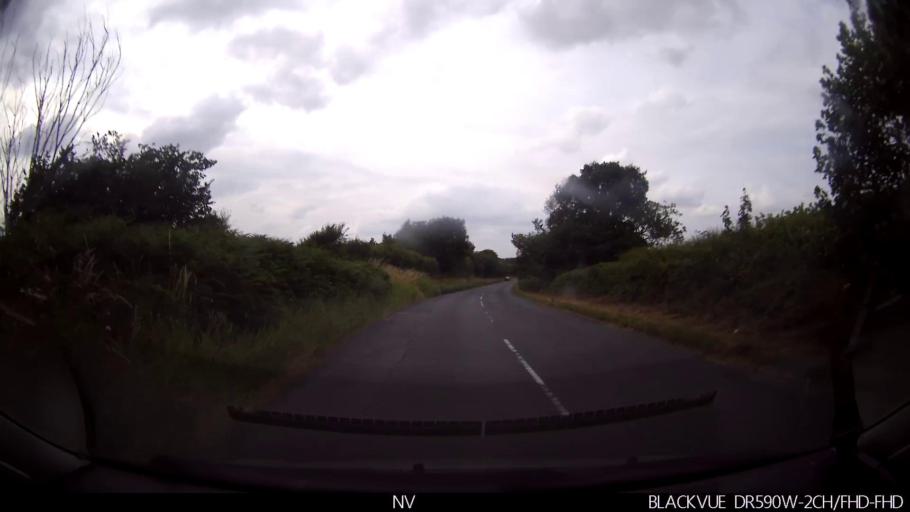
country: GB
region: England
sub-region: City of York
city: Holtby
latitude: 54.0408
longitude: -0.9557
